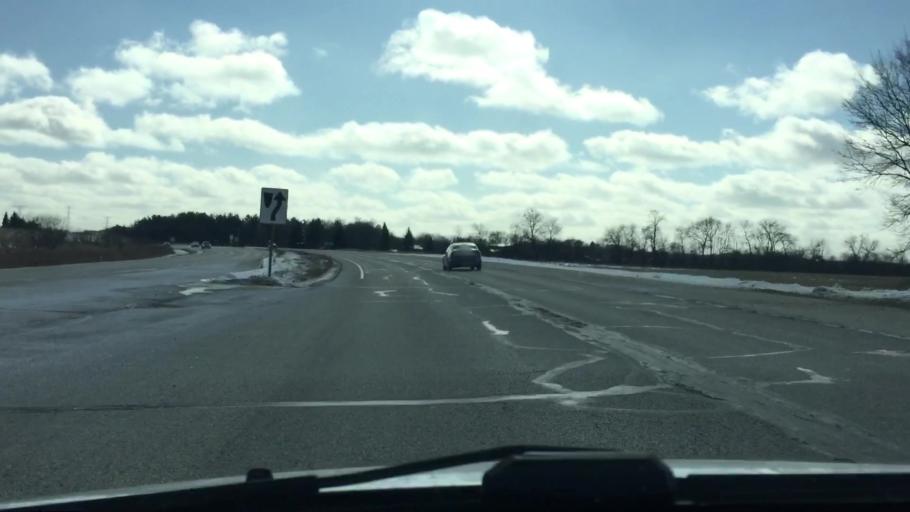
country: US
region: Wisconsin
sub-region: Waukesha County
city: Big Bend
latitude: 42.9263
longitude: -88.2289
